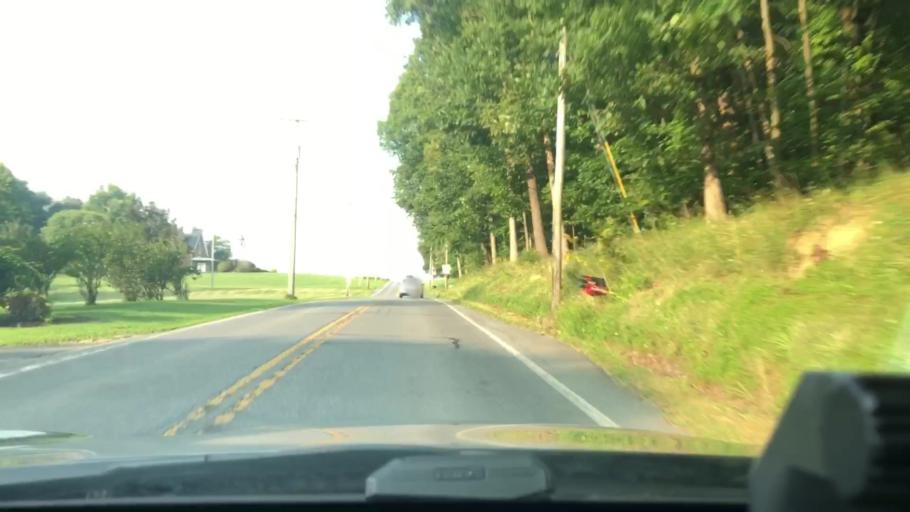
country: US
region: Pennsylvania
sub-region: Berks County
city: Kutztown
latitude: 40.5733
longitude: -75.8048
